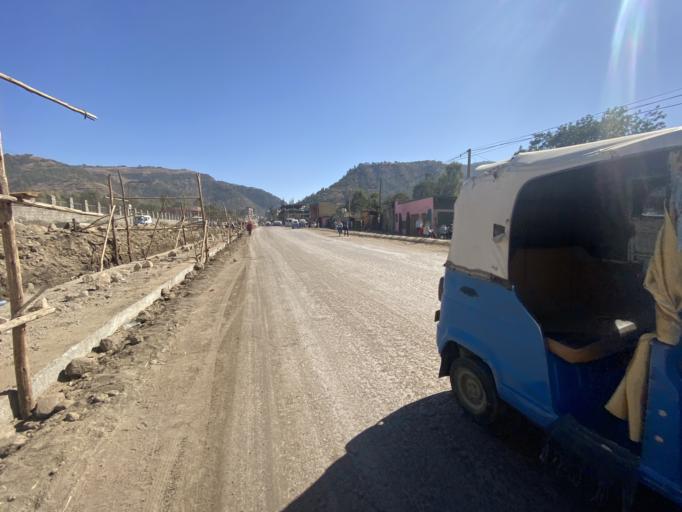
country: ET
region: Amhara
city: Robit
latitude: 11.8276
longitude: 39.5961
